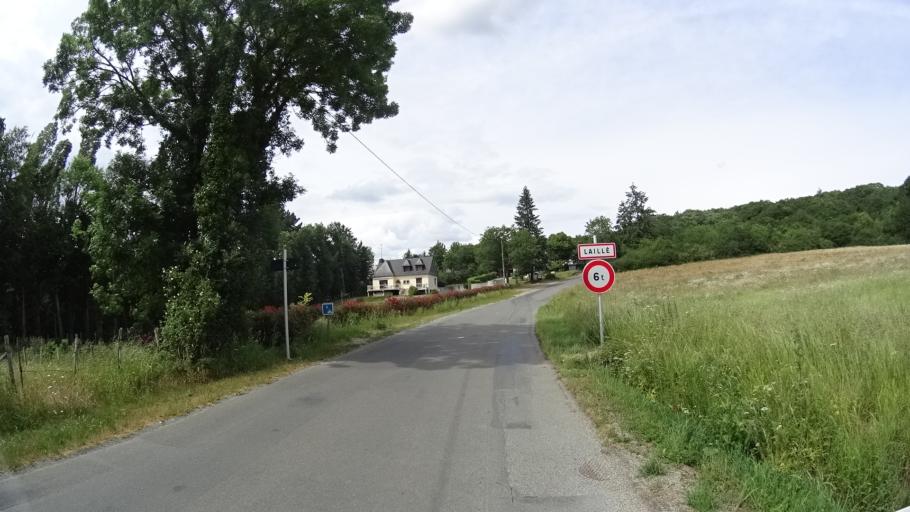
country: FR
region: Brittany
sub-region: Departement d'Ille-et-Vilaine
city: Laille
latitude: 47.9698
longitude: -1.7240
